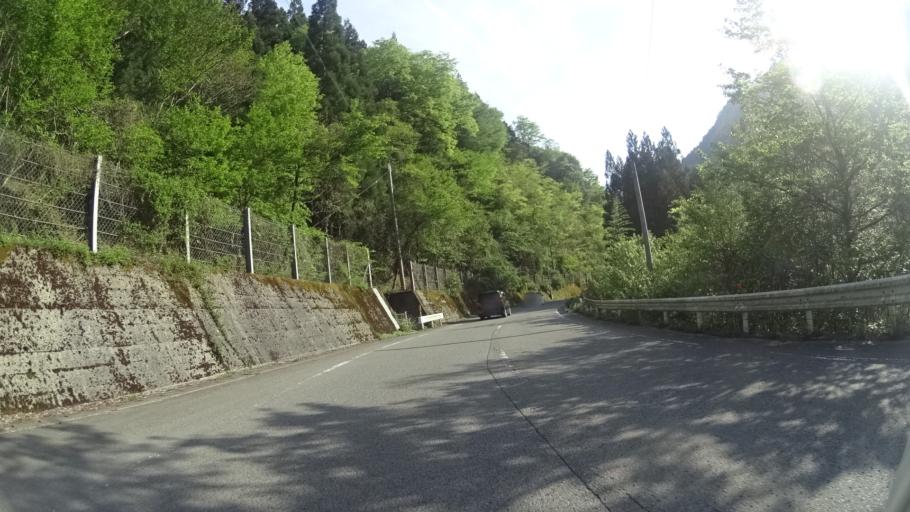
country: JP
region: Tokushima
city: Ikedacho
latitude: 33.8665
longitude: 133.9045
